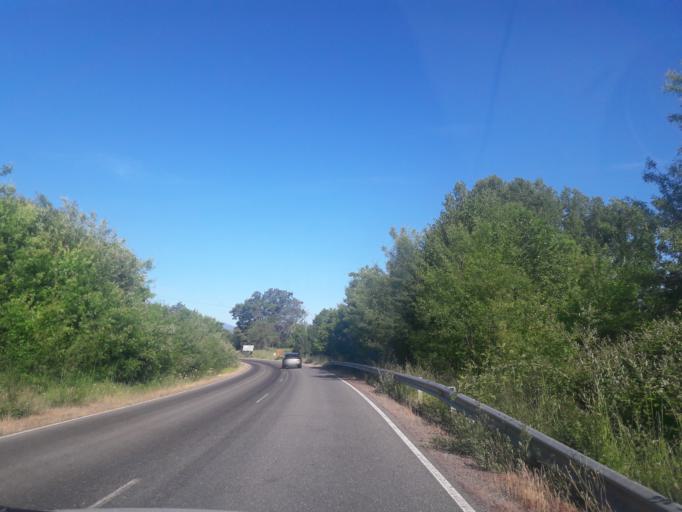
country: ES
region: Castille and Leon
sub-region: Provincia de Salamanca
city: Penacaballera
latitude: 40.3434
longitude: -5.8631
